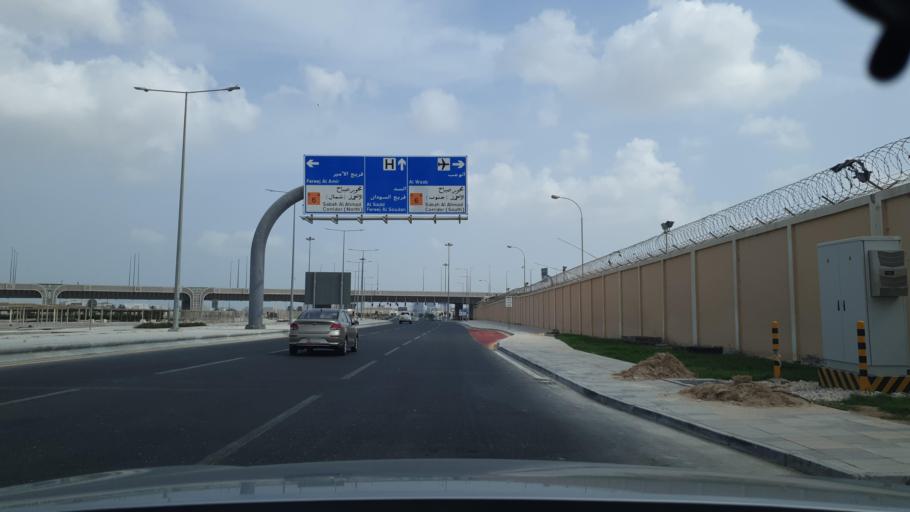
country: QA
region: Baladiyat ar Rayyan
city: Ar Rayyan
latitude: 25.2784
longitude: 51.4693
